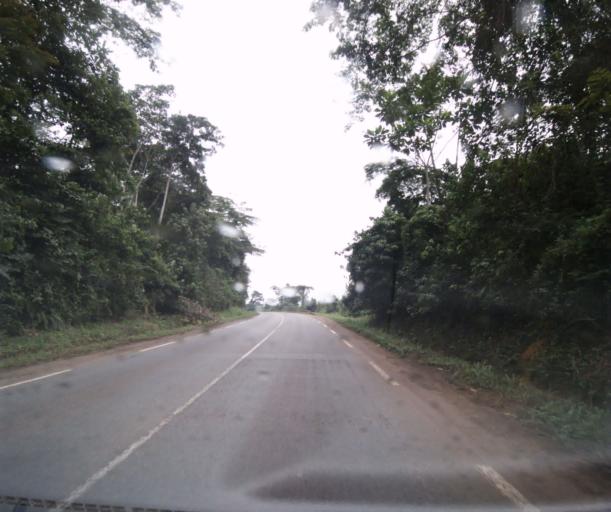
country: CM
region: Centre
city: Mbankomo
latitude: 3.7736
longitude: 11.1527
